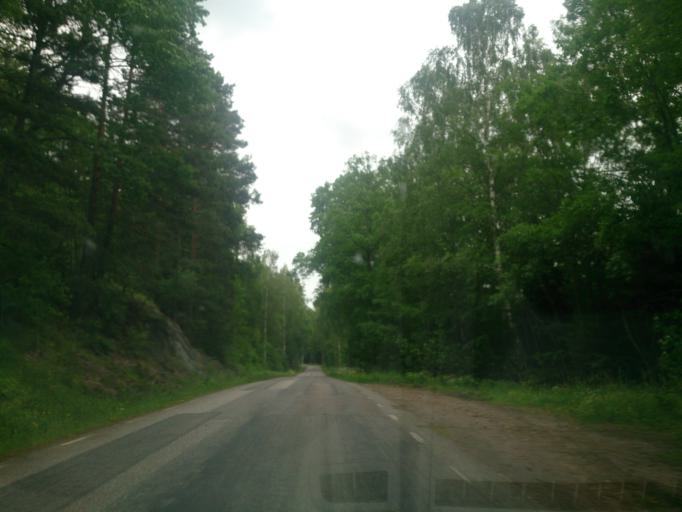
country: SE
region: OEstergoetland
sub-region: Soderkopings Kommun
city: Soederkoeping
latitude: 58.3059
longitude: 16.2769
